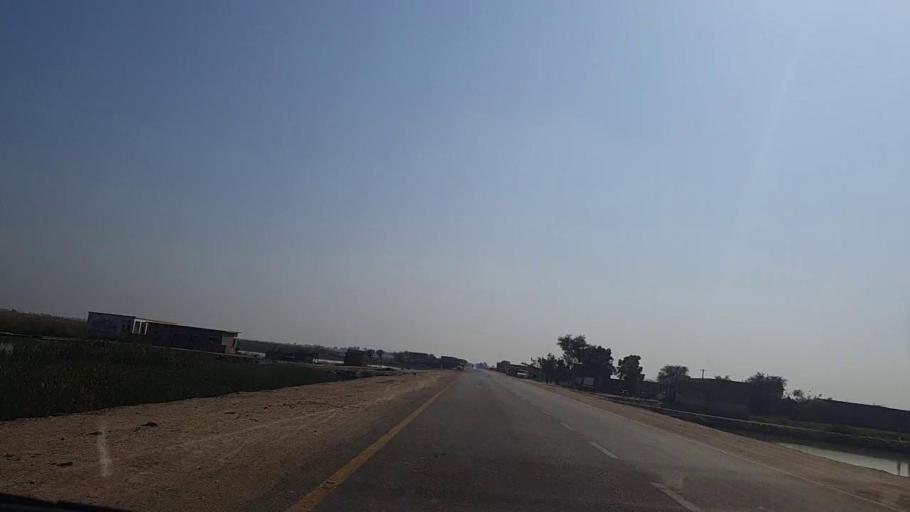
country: PK
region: Sindh
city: Sakrand
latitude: 26.0753
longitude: 68.4047
